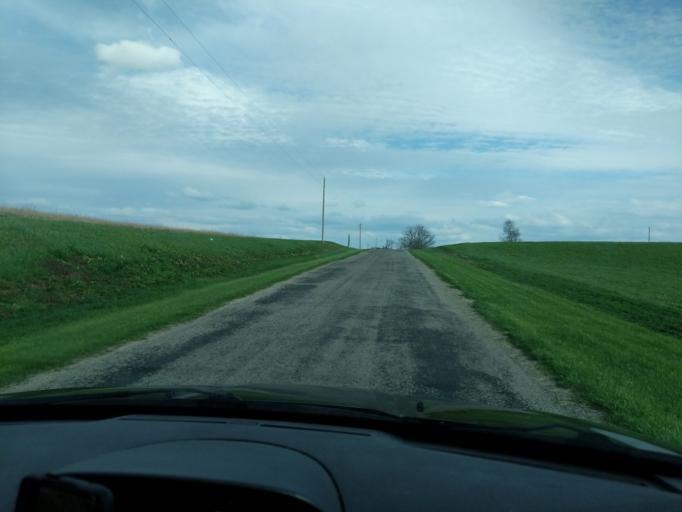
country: US
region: Ohio
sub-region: Champaign County
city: North Lewisburg
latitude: 40.1965
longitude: -83.6563
